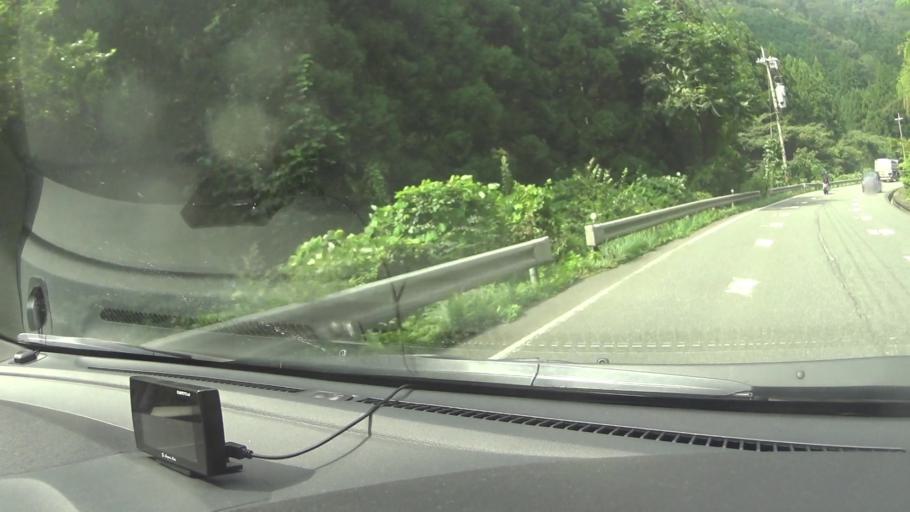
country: JP
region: Kyoto
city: Ayabe
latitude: 35.2399
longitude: 135.2984
